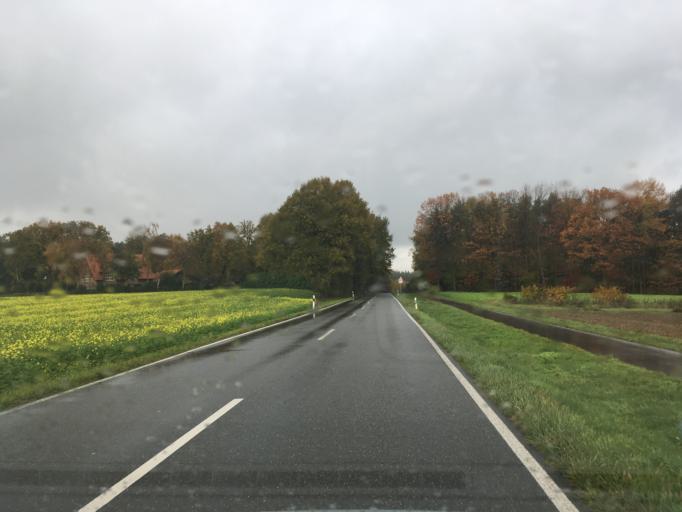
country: DE
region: North Rhine-Westphalia
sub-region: Regierungsbezirk Munster
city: Klein Reken
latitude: 51.8381
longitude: 7.0331
